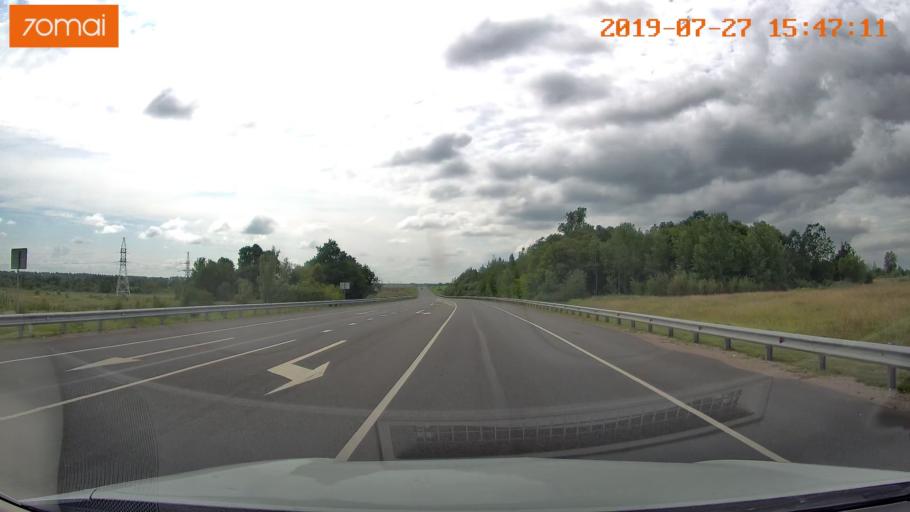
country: RU
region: Kaliningrad
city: Gusev
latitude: 54.6029
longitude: 22.0941
